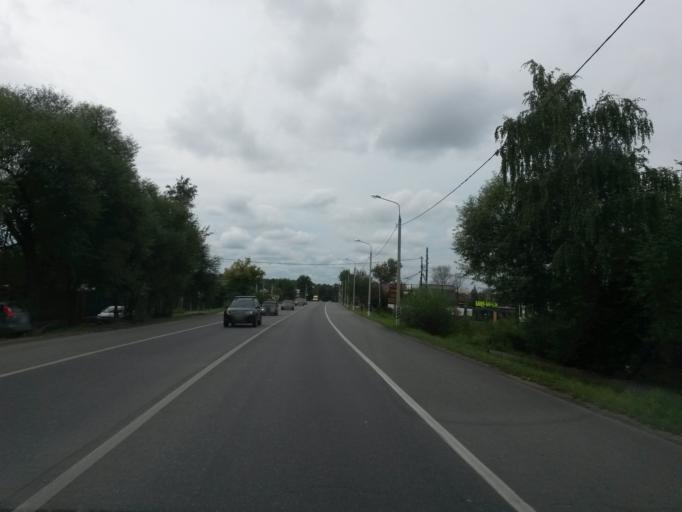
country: RU
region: Moskovskaya
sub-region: Chekhovskiy Rayon
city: Chekhov
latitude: 55.1845
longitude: 37.4952
